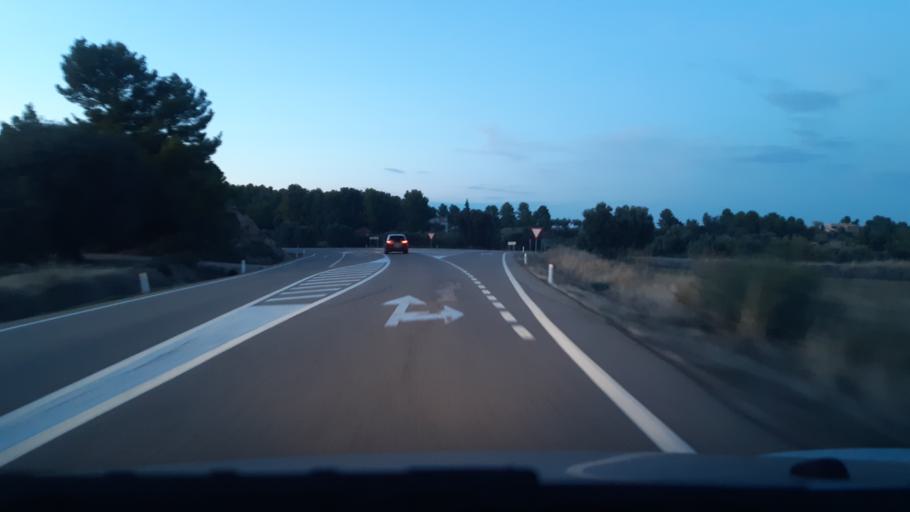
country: ES
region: Aragon
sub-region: Provincia de Teruel
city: Calaceite
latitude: 40.9778
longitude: 0.2026
